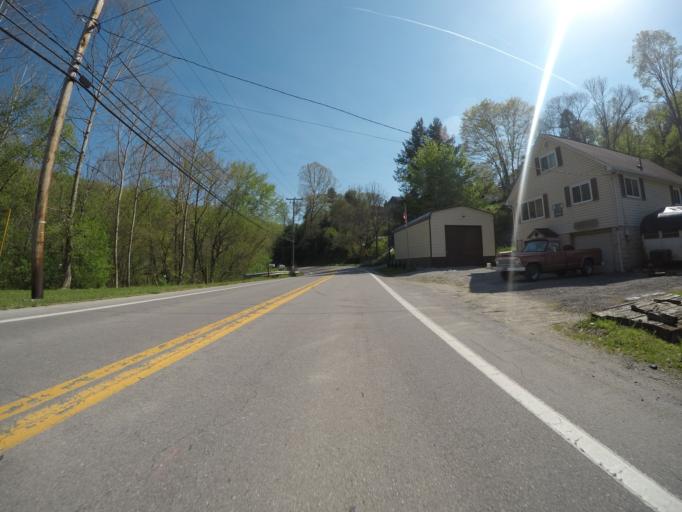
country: US
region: West Virginia
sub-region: Kanawha County
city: Clendenin
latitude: 38.5007
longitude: -81.3485
